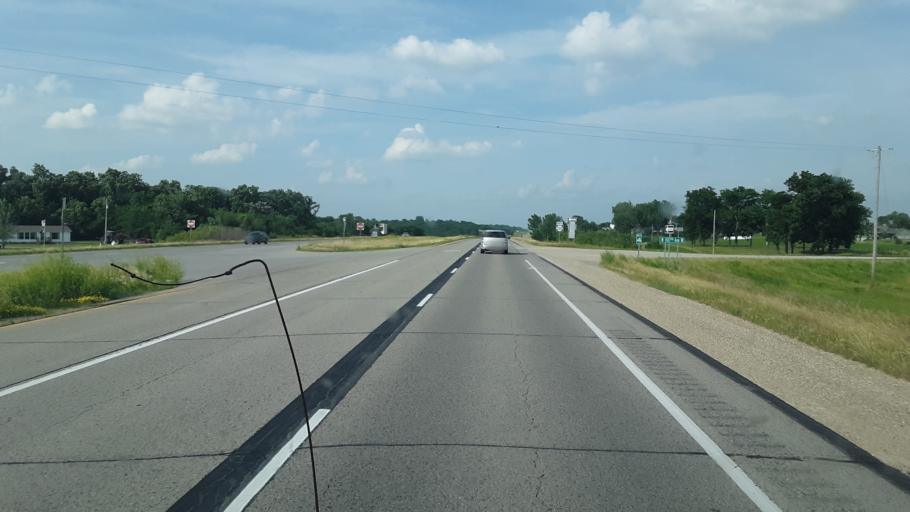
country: US
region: Iowa
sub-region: Jasper County
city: Baxter
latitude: 41.8485
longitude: -93.2538
